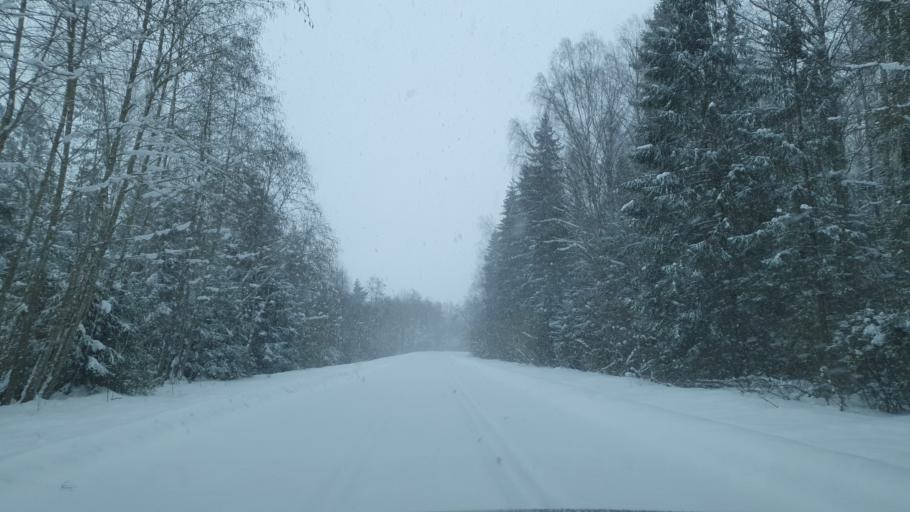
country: EE
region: Jogevamaa
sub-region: Jogeva linn
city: Jogeva
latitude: 58.8047
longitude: 26.4397
